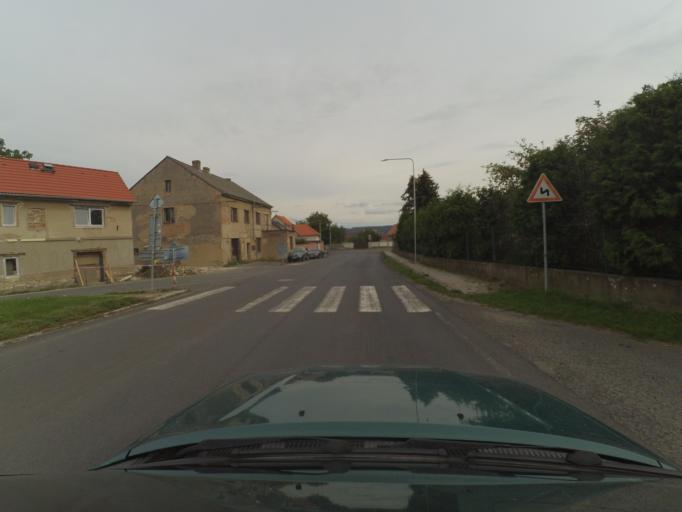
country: CZ
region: Ustecky
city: Peruc
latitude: 50.4039
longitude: 13.9413
